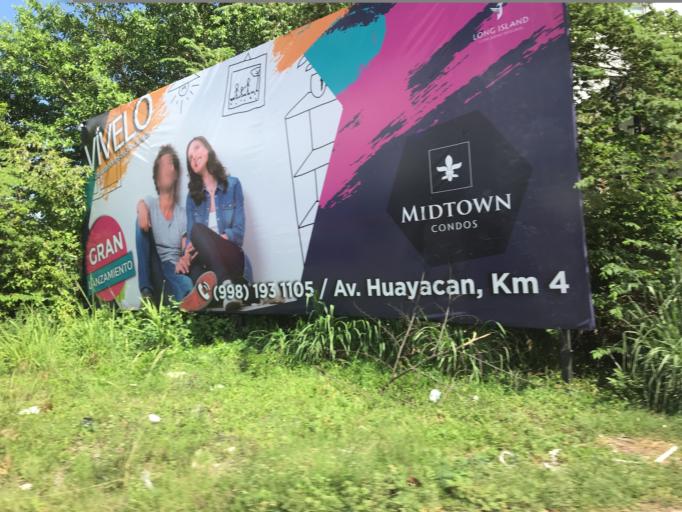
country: MX
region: Quintana Roo
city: Cancun
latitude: 21.1540
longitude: -86.8212
